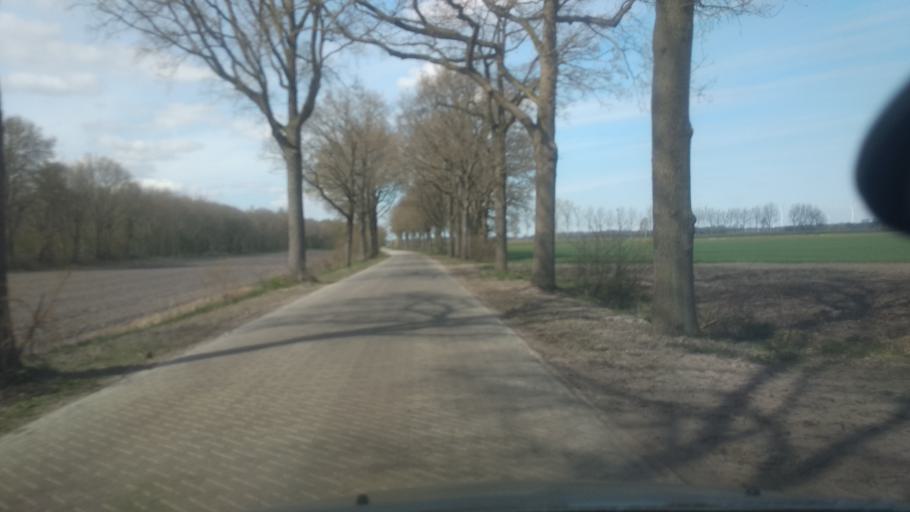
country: NL
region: Drenthe
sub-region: Gemeente Borger-Odoorn
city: Borger
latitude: 52.9576
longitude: 6.8243
